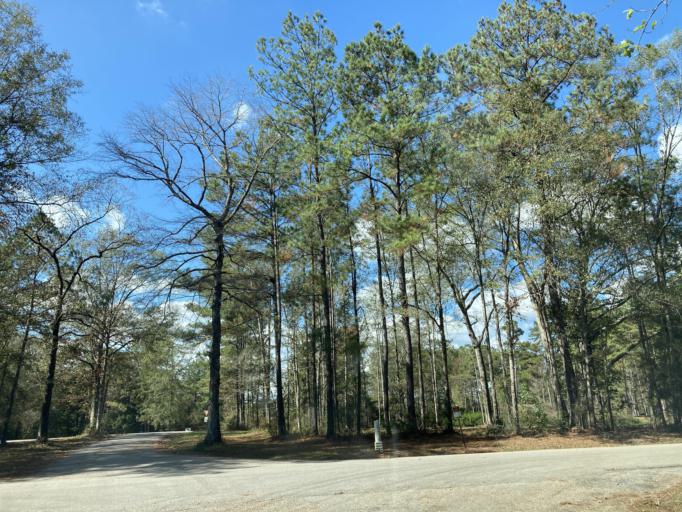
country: US
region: Mississippi
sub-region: Lamar County
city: Purvis
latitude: 31.2367
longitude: -89.4332
